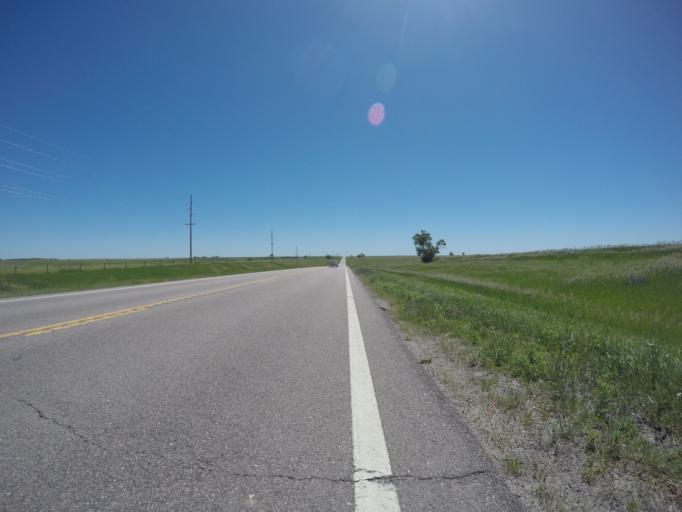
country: US
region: Kansas
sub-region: Norton County
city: Norton
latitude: 39.8284
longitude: -99.6551
